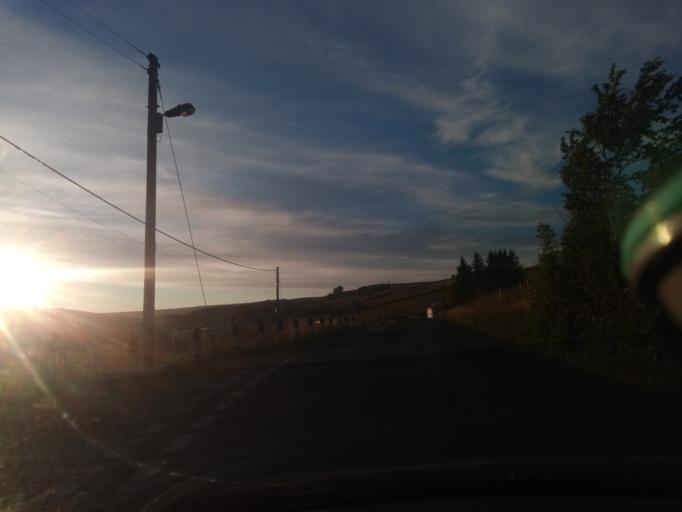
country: GB
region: England
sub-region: County Durham
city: Holwick
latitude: 54.7632
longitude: -2.2321
